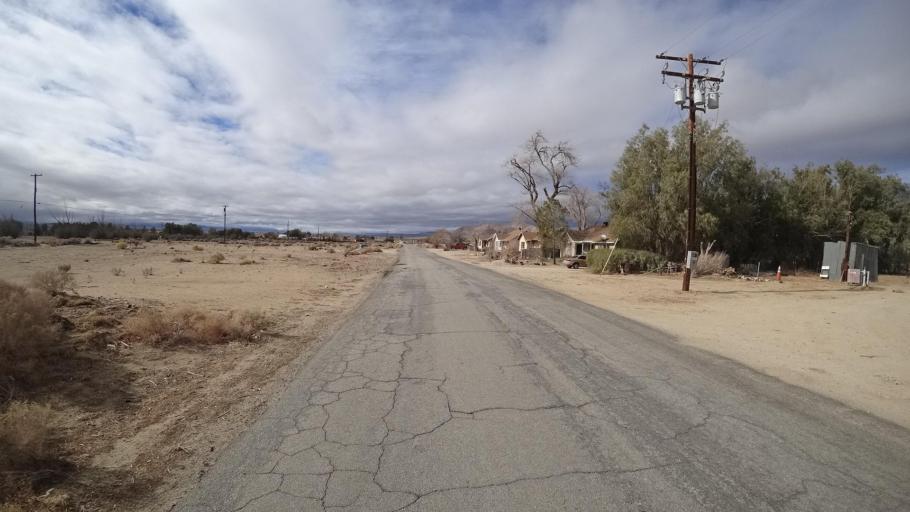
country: US
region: California
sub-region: Kern County
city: Rosamond
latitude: 34.8710
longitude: -118.2307
